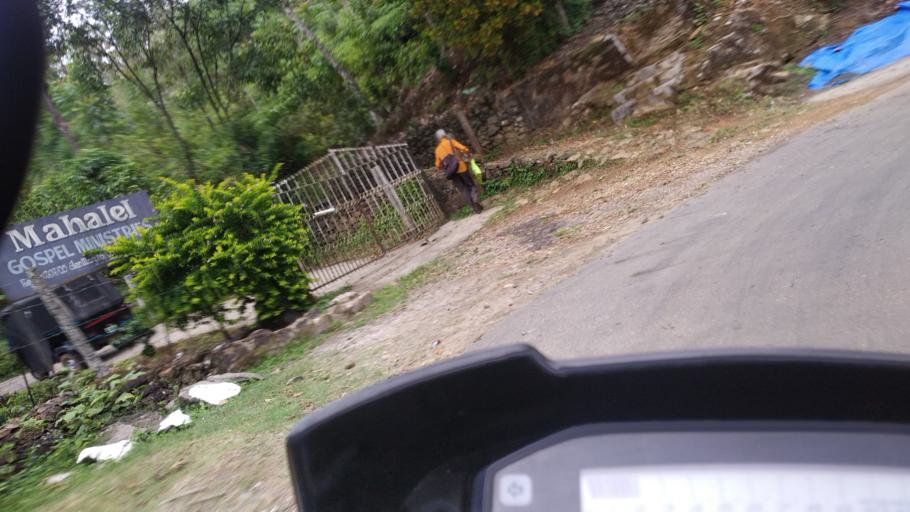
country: IN
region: Kerala
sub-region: Kottayam
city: Erattupetta
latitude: 9.5880
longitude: 77.0093
